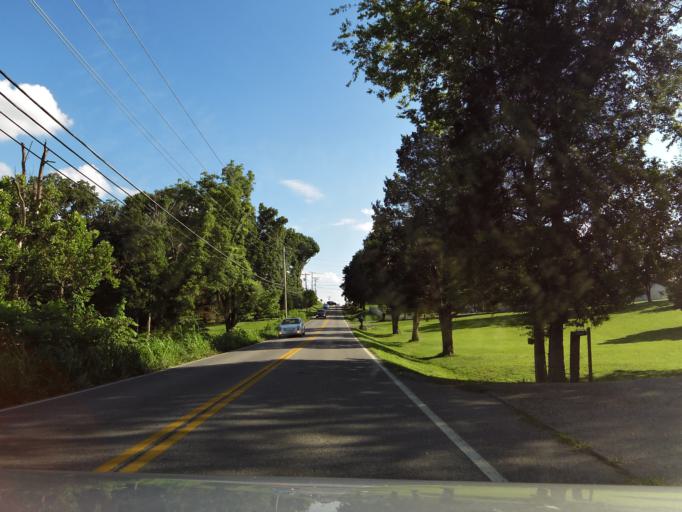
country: US
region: Tennessee
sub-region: Blount County
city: Louisville
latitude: 35.7716
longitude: -84.0276
